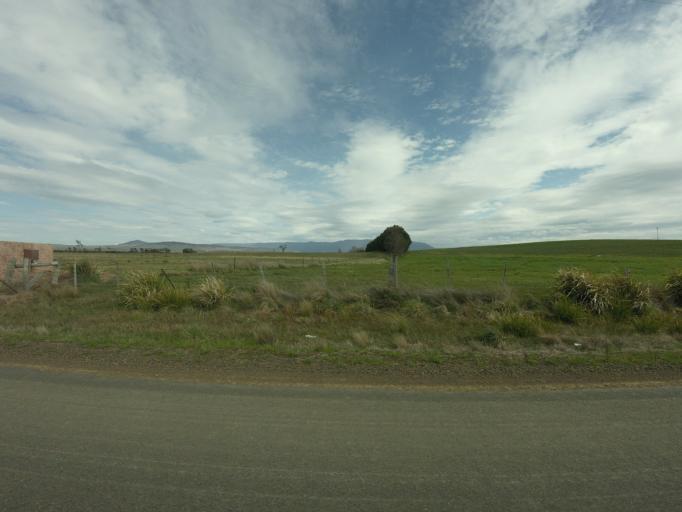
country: AU
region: Tasmania
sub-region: Northern Midlands
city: Evandale
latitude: -41.8259
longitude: 147.3199
